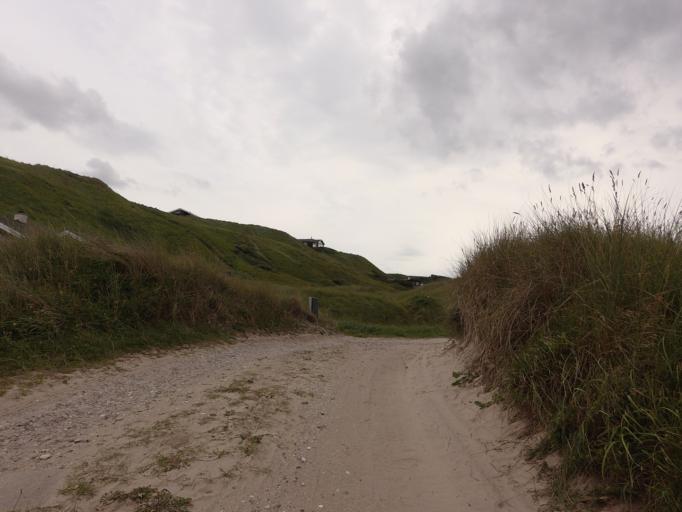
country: DK
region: North Denmark
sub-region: Jammerbugt Kommune
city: Pandrup
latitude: 57.3079
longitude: 9.6469
